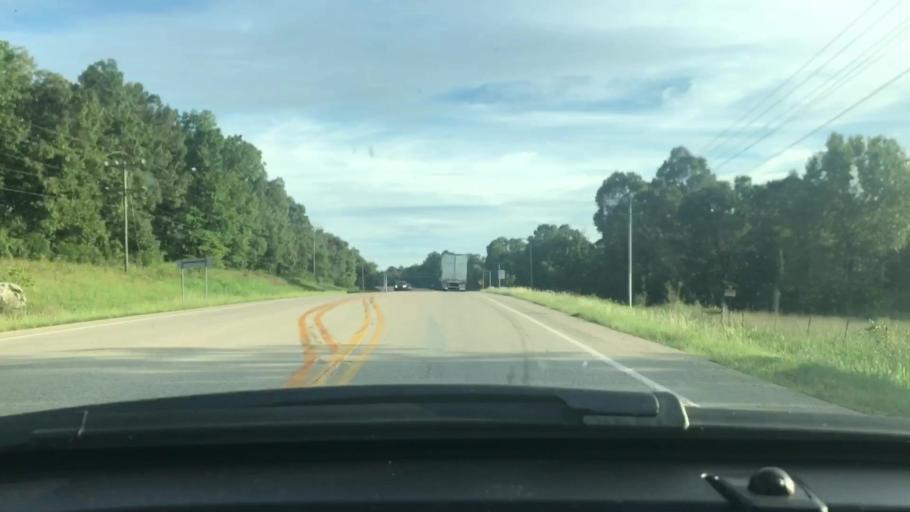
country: US
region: Arkansas
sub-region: Lawrence County
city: Hoxie
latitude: 36.1346
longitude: -91.1583
